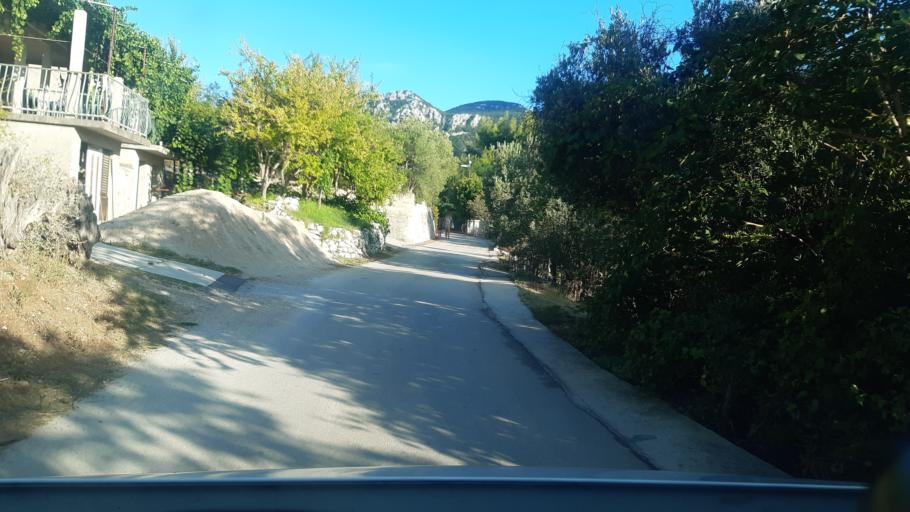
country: HR
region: Dubrovacko-Neretvanska
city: Blato
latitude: 42.8906
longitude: 17.4574
